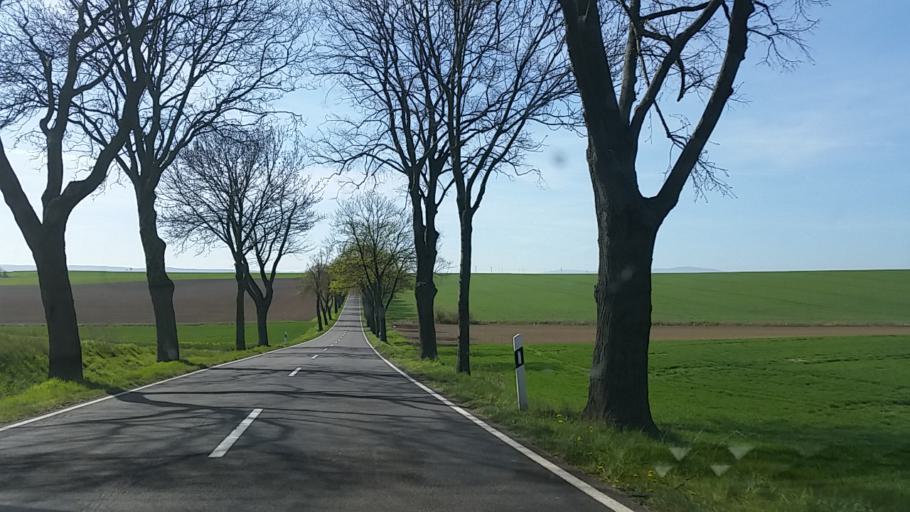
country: DE
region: Lower Saxony
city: Jerxheim
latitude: 52.0801
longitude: 10.8945
